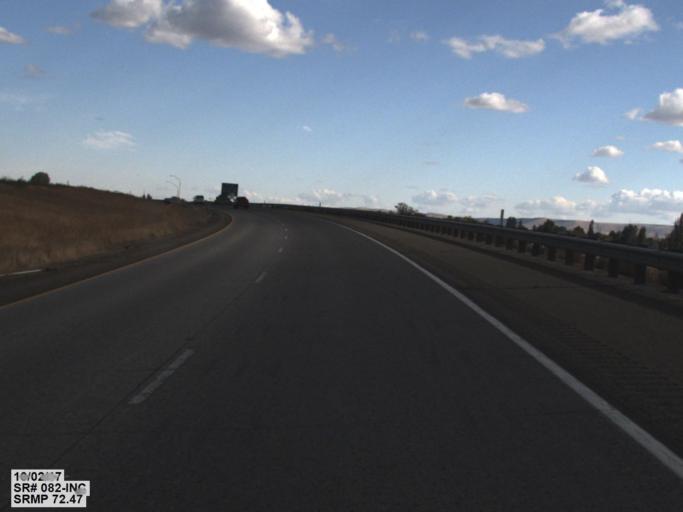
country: US
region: Washington
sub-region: Yakima County
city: Grandview
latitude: 46.2713
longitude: -119.9268
